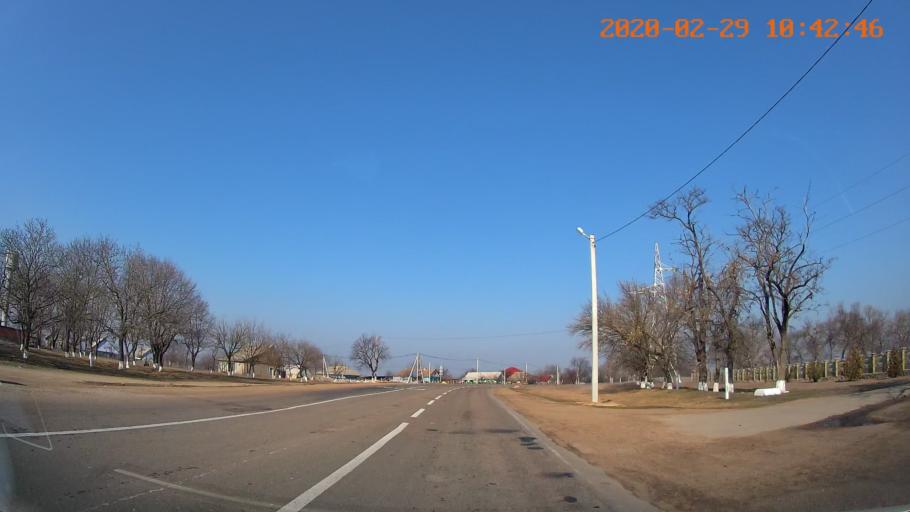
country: MD
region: Telenesti
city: Grigoriopol
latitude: 47.0542
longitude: 29.4070
